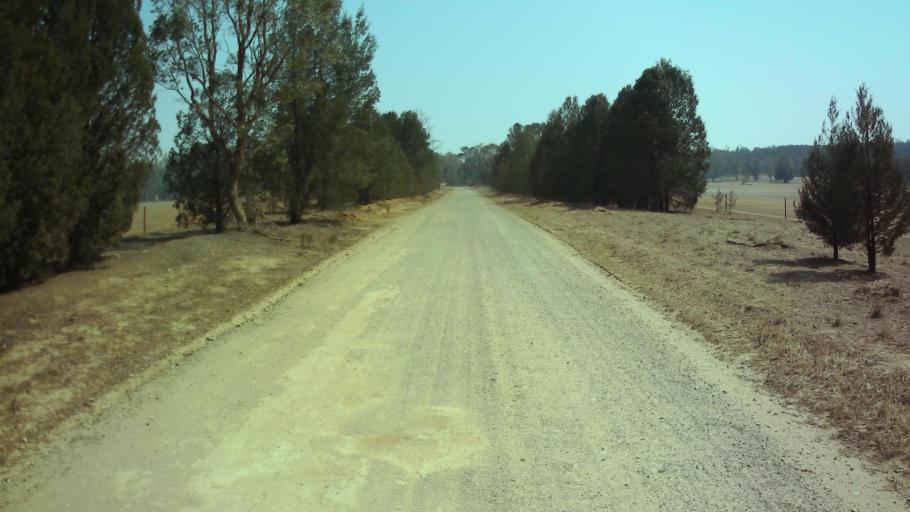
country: AU
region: New South Wales
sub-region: Weddin
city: Grenfell
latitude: -33.6697
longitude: 148.2749
